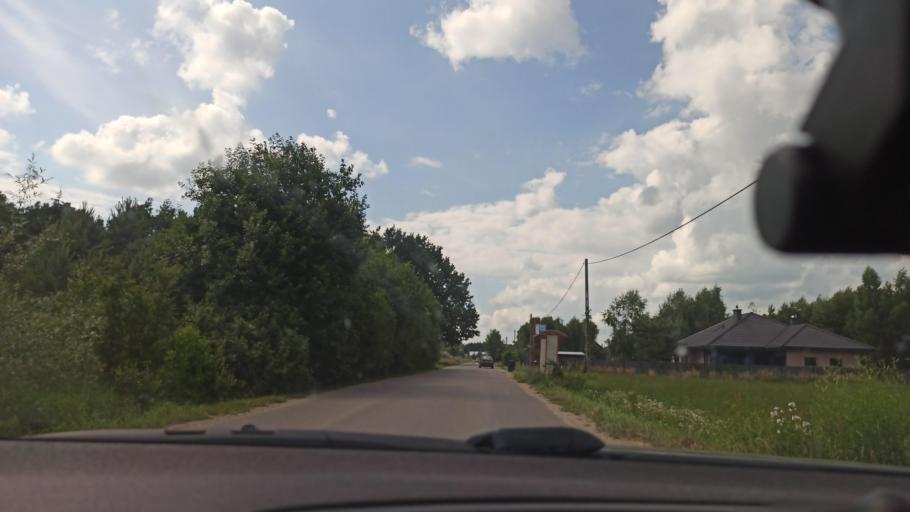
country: PL
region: Podlasie
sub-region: Powiat bialostocki
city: Turosn Koscielna
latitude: 53.0655
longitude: 23.0935
